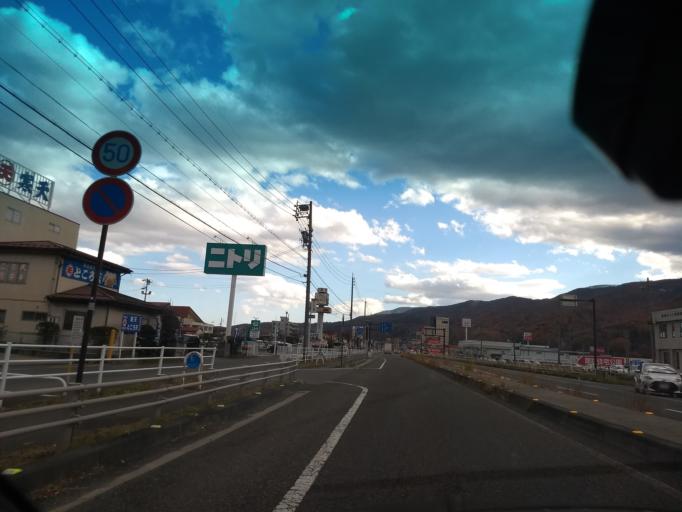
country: JP
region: Nagano
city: Chino
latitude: 36.0075
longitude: 138.1305
